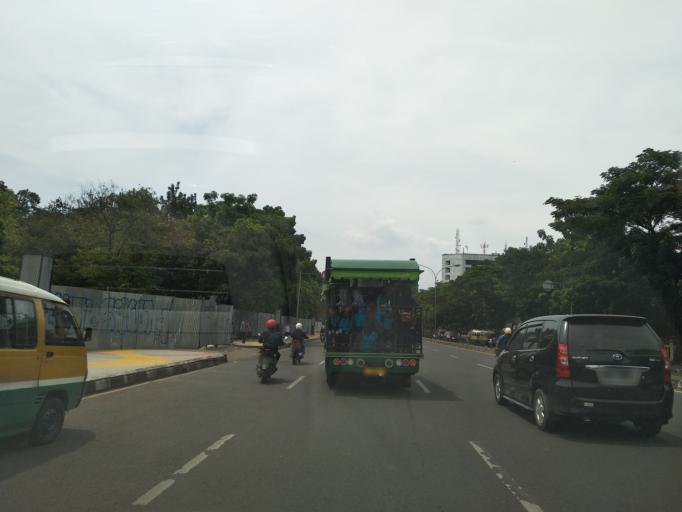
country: ID
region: West Java
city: Bandung
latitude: -6.9374
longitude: 107.6046
